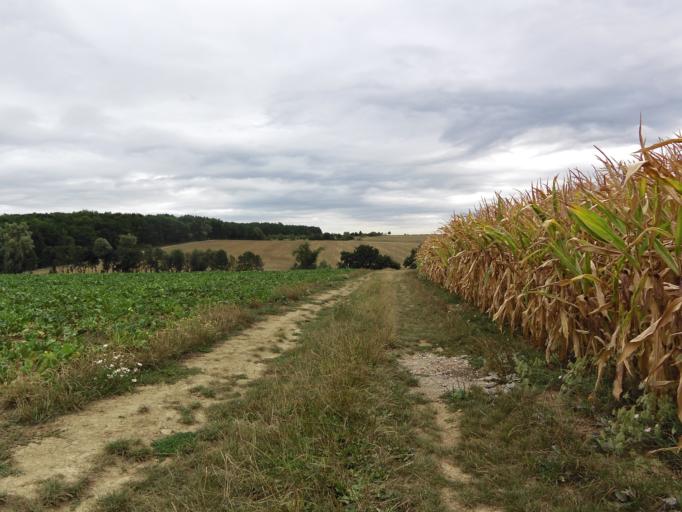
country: DE
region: Bavaria
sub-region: Regierungsbezirk Unterfranken
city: Rimpar
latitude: 49.8410
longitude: 9.9663
